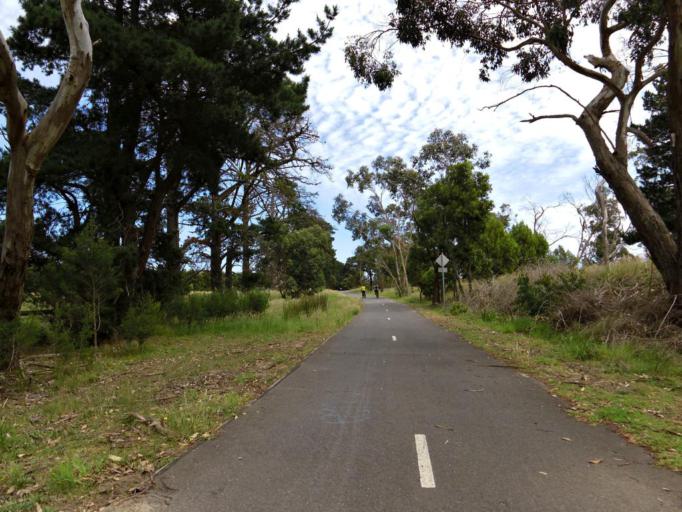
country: AU
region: Victoria
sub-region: Mornington Peninsula
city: Moorooduc
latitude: -38.2095
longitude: 145.1292
